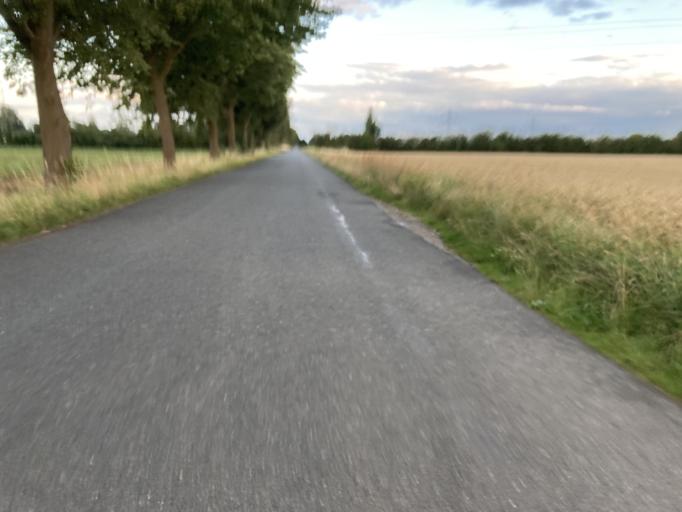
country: DE
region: Lower Saxony
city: Verden
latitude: 52.9274
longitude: 9.2005
